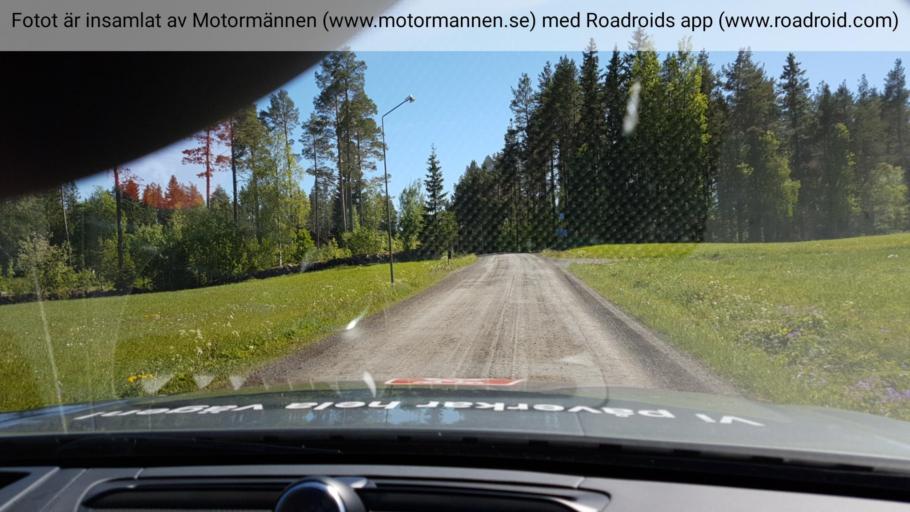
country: SE
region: Jaemtland
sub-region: OEstersunds Kommun
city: Brunflo
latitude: 62.9941
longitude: 14.8072
